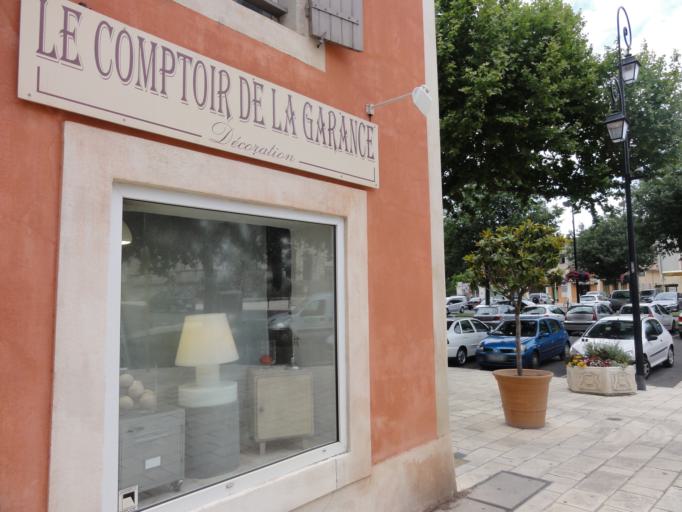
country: FR
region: Provence-Alpes-Cote d'Azur
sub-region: Departement du Vaucluse
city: Orange
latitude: 44.1351
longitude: 4.8052
